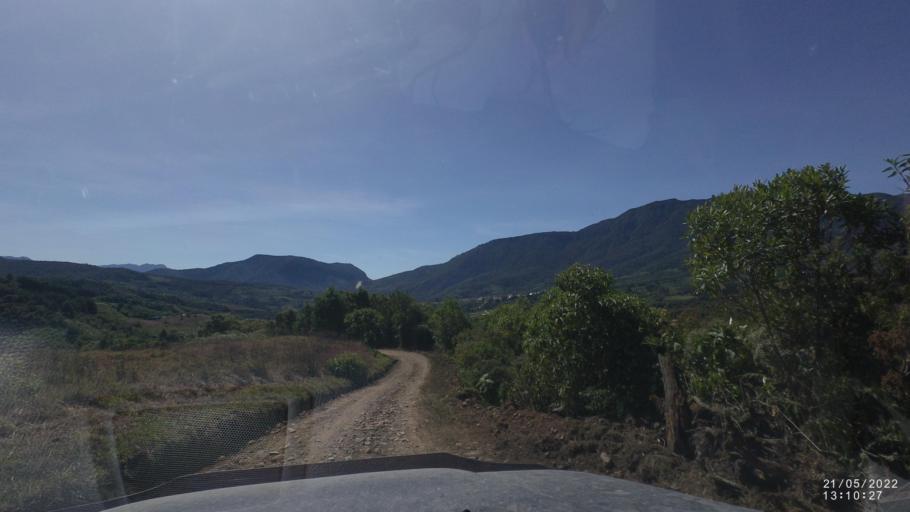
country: BO
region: Cochabamba
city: Colomi
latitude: -17.1409
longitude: -65.9421
